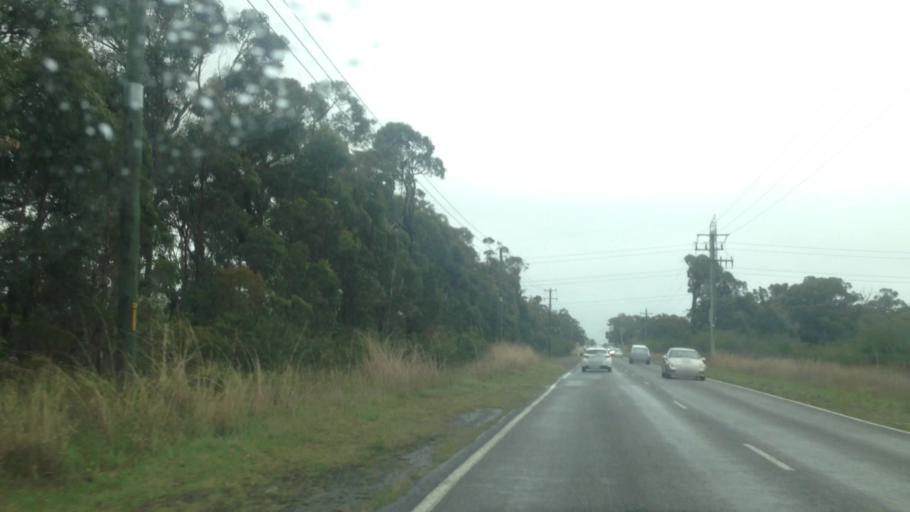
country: AU
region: New South Wales
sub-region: Wyong Shire
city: Charmhaven
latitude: -33.1603
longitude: 151.4785
